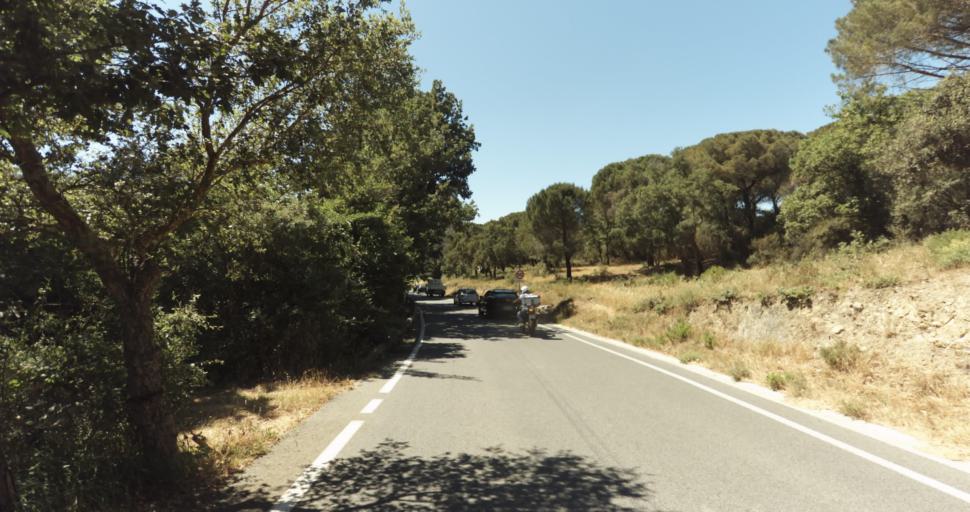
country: FR
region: Provence-Alpes-Cote d'Azur
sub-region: Departement du Var
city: Gassin
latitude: 43.2377
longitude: 6.5710
